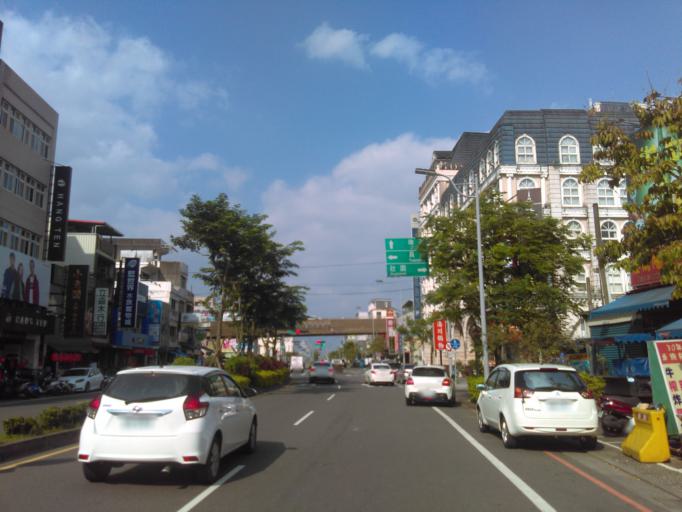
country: TW
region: Taiwan
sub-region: Yilan
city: Yilan
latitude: 24.7572
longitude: 121.7586
